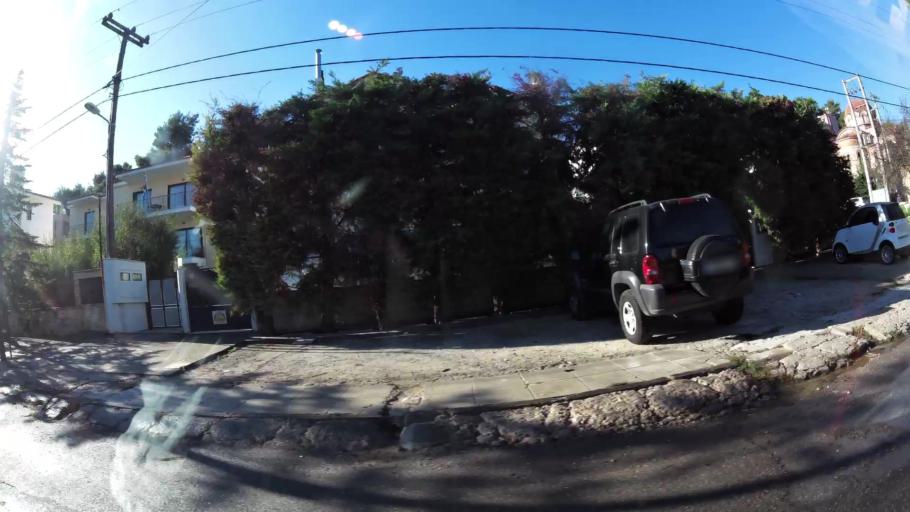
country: GR
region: Attica
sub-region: Nomarchia Anatolikis Attikis
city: Stamata
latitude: 38.1359
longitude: 23.8749
